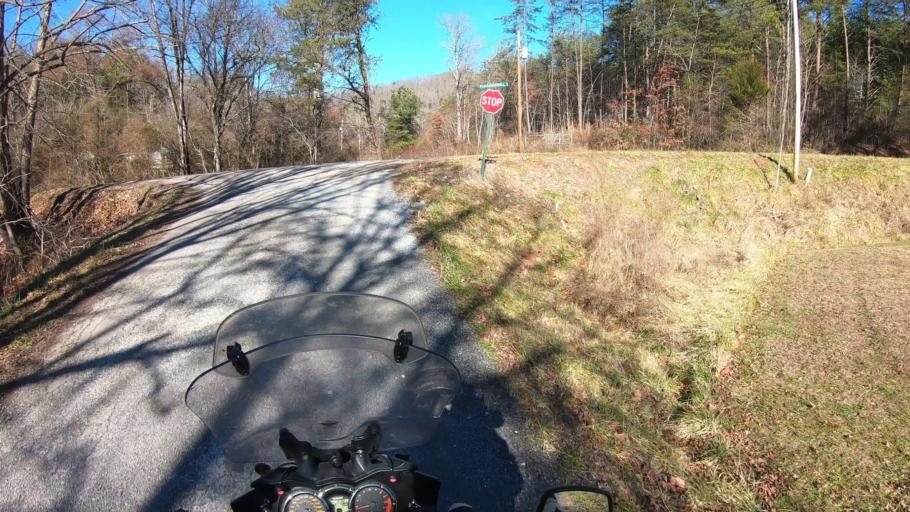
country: US
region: Georgia
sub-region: Fannin County
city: McCaysville
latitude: 34.9991
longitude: -84.3288
